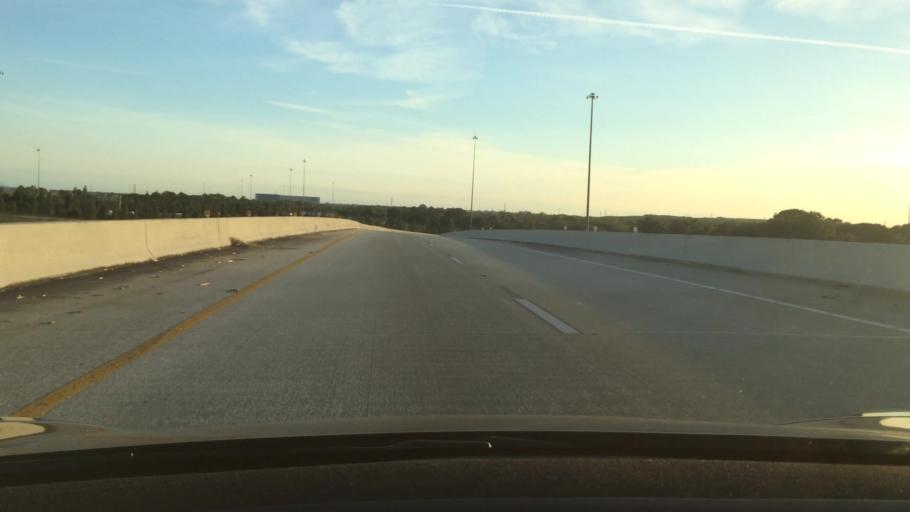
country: US
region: Florida
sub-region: Pinellas County
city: Feather Sound
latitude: 27.8798
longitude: -82.6623
